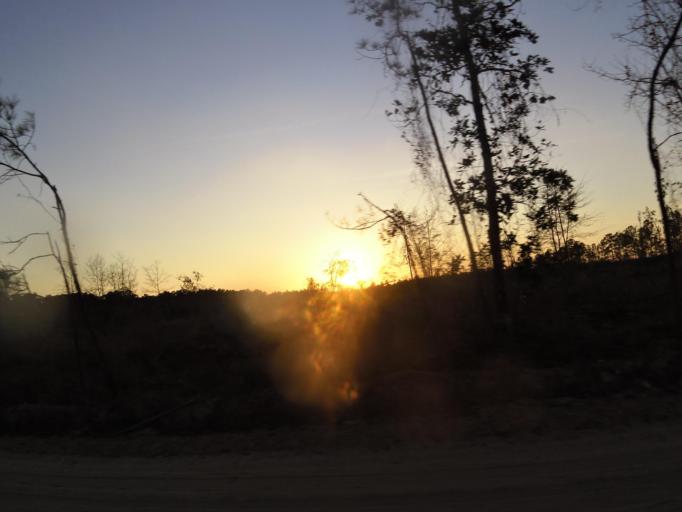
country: US
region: Florida
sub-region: Clay County
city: Green Cove Springs
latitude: 29.9090
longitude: -81.7804
